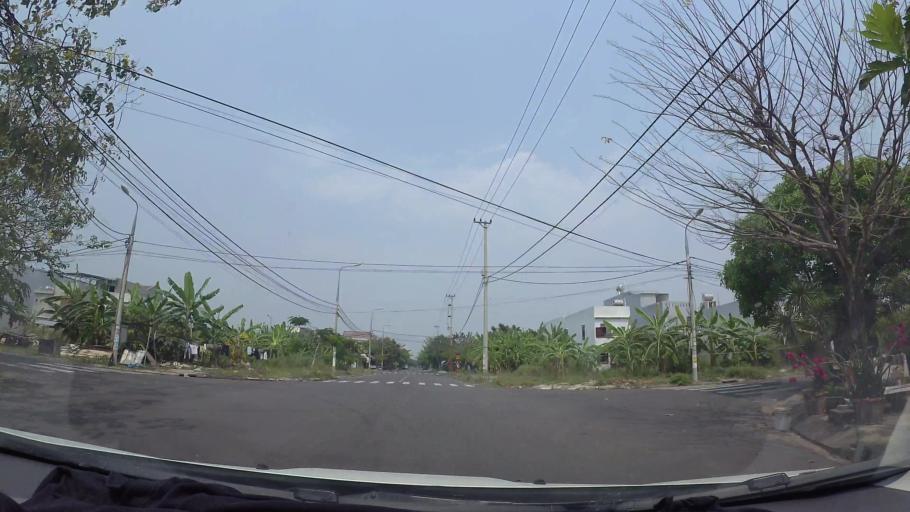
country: VN
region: Da Nang
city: Cam Le
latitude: 16.0001
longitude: 108.2201
